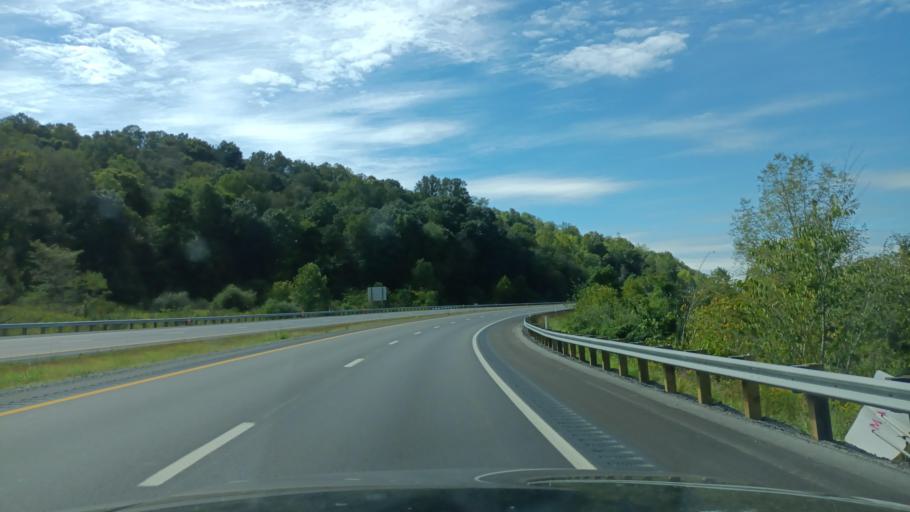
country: US
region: West Virginia
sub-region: Harrison County
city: Clarksburg
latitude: 39.2870
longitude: -80.3797
